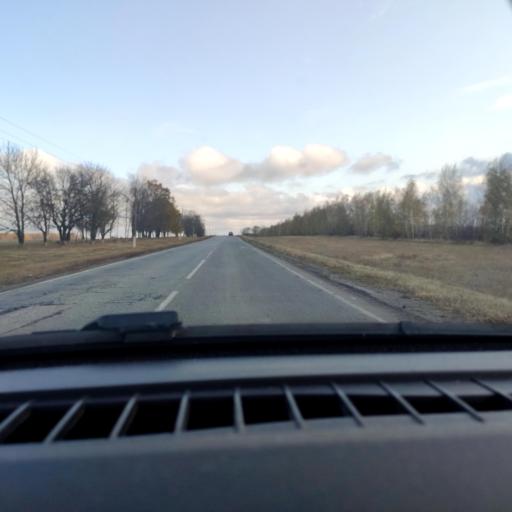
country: RU
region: Belgorod
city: Ilovka
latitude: 50.7140
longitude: 38.6653
